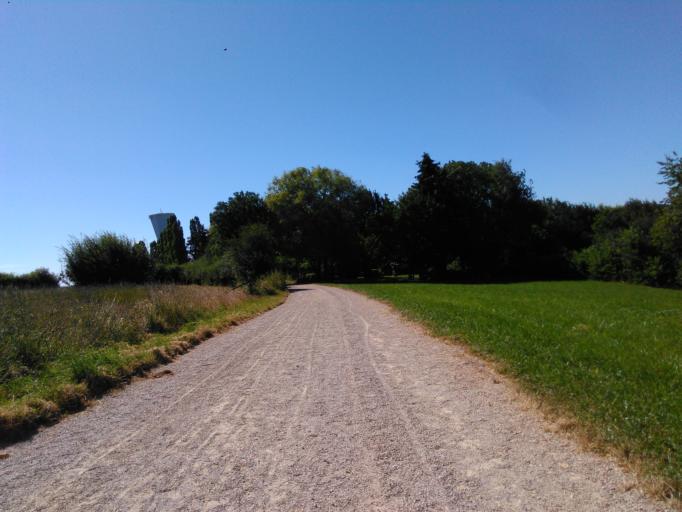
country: LU
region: Luxembourg
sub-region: Canton d'Esch-sur-Alzette
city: Reckange-sur-Mess
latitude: 49.5623
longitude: 6.0177
